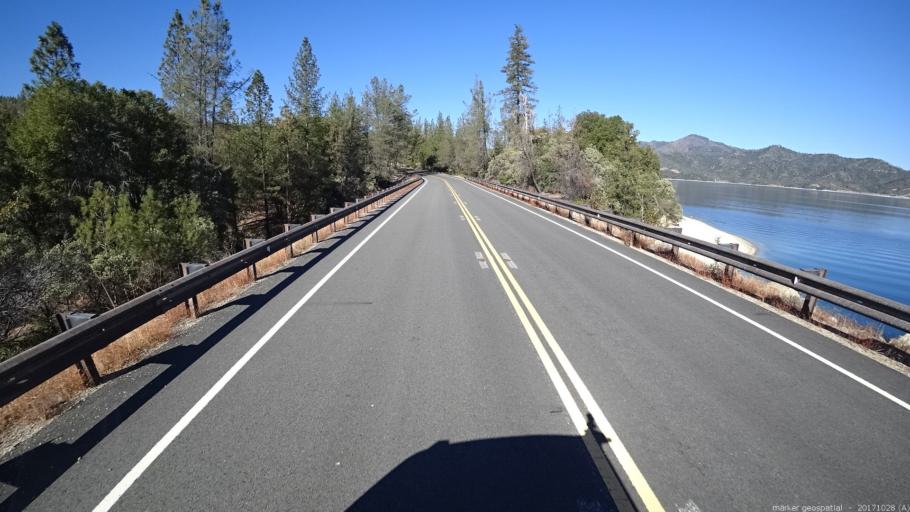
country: US
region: California
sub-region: Shasta County
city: Shasta
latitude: 40.6003
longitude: -122.5480
